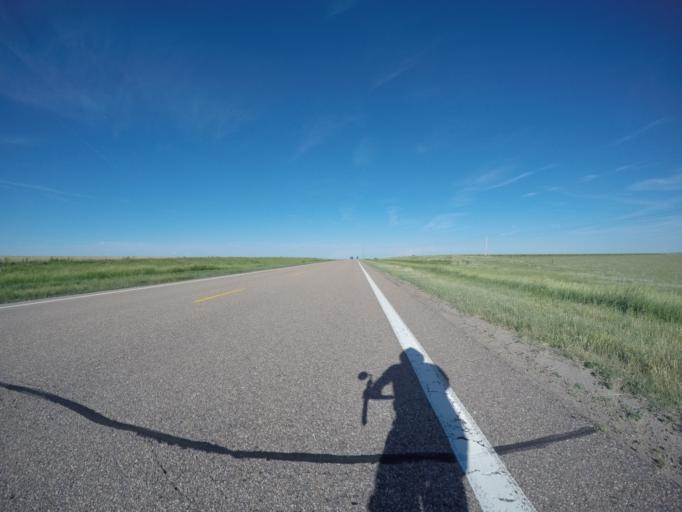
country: US
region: Kansas
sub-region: Cheyenne County
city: Saint Francis
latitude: 39.7571
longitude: -101.8904
